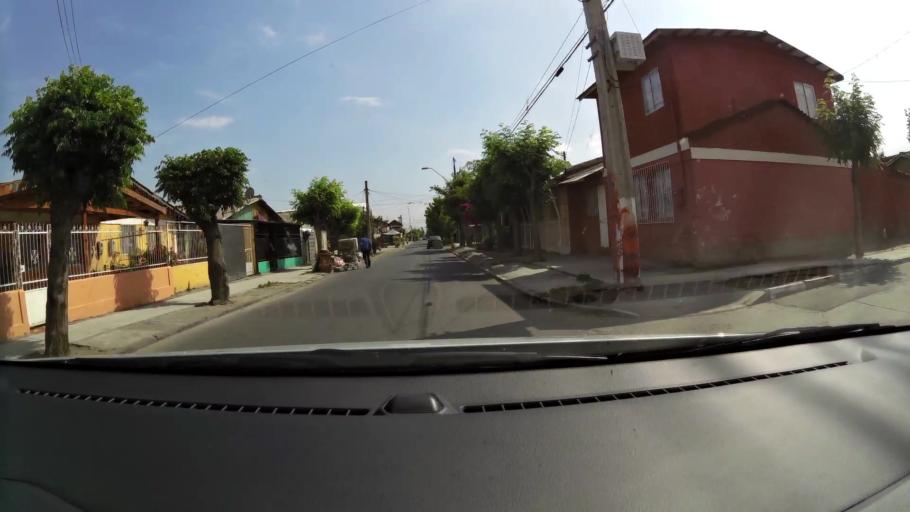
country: CL
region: Santiago Metropolitan
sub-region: Provincia de Santiago
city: Santiago
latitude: -33.5145
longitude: -70.6955
